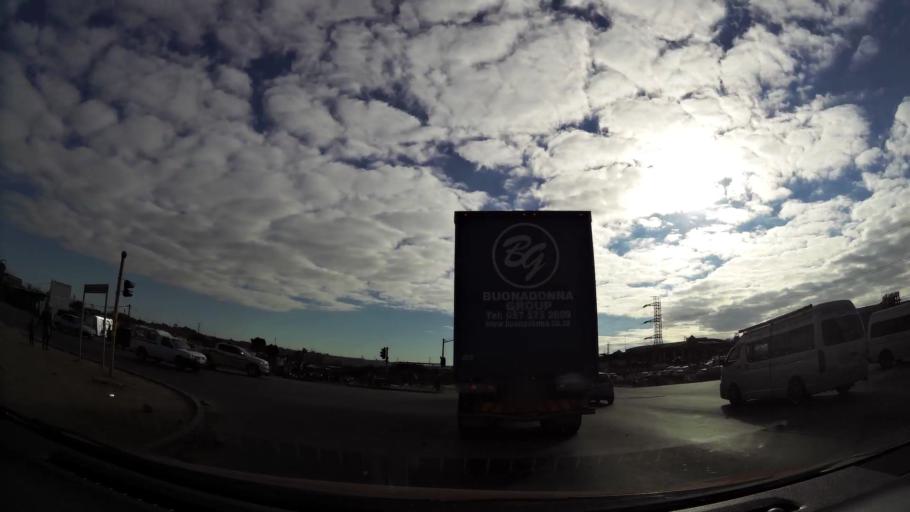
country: ZA
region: Gauteng
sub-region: Ekurhuleni Metropolitan Municipality
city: Tembisa
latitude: -26.0373
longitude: 28.1902
